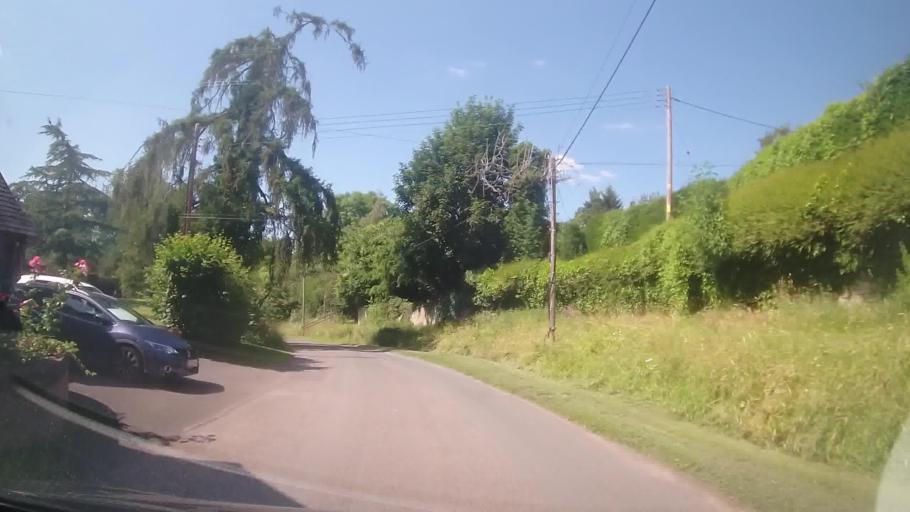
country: GB
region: England
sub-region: Herefordshire
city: Ocle Pychard
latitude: 52.0623
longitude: -2.5585
